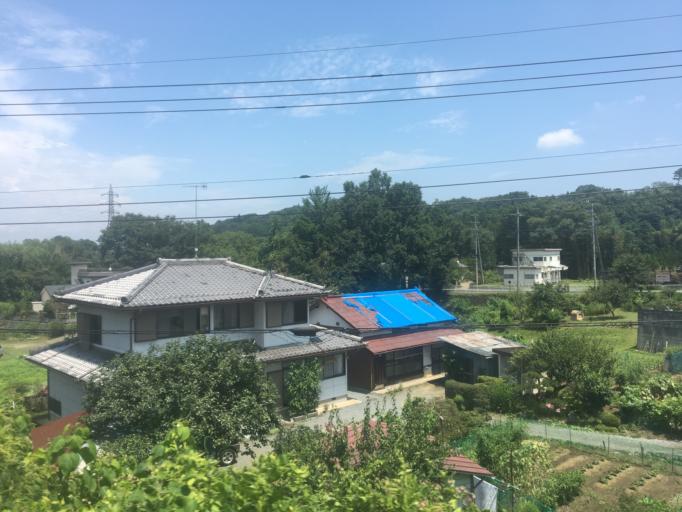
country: JP
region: Saitama
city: Yorii
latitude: 36.0978
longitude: 139.1941
